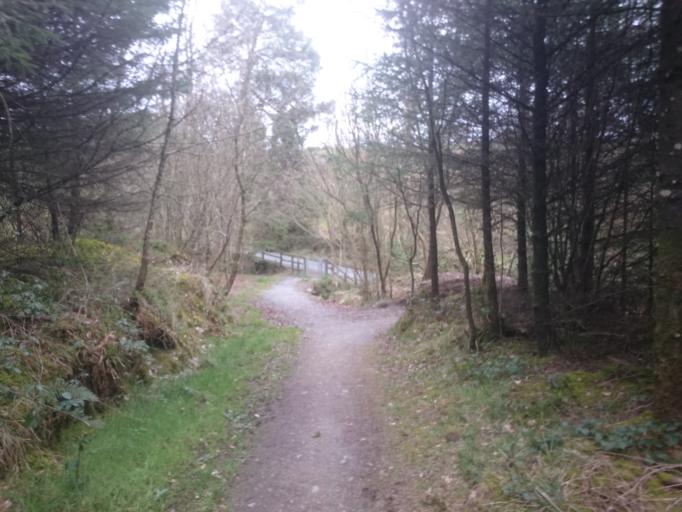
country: IE
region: Leinster
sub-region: Kilkenny
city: Callan
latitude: 52.6552
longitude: -7.5448
